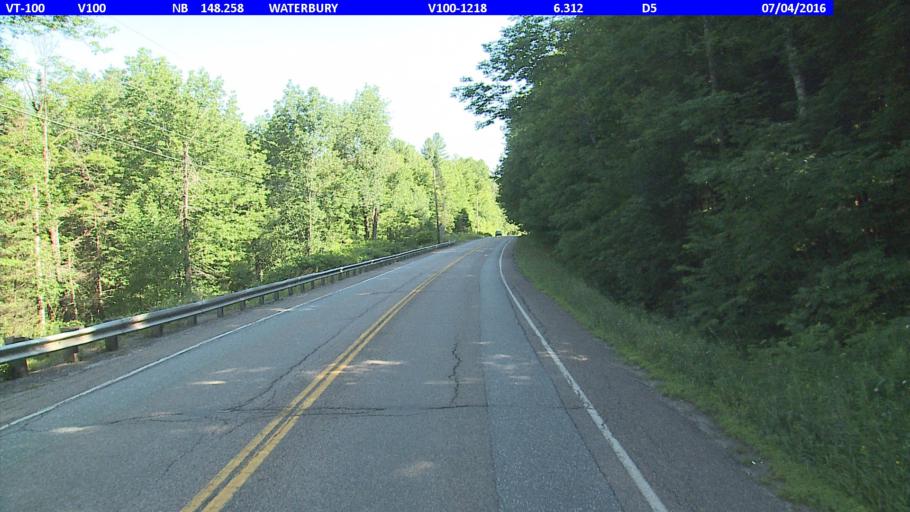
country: US
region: Vermont
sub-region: Washington County
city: Waterbury
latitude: 44.4195
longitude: -72.7226
